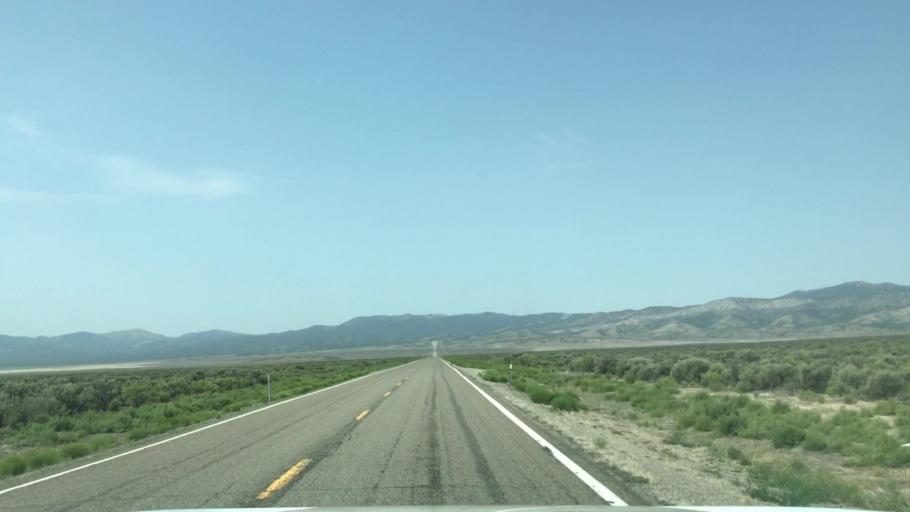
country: US
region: Nevada
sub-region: White Pine County
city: Ely
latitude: 39.0582
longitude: -114.4843
